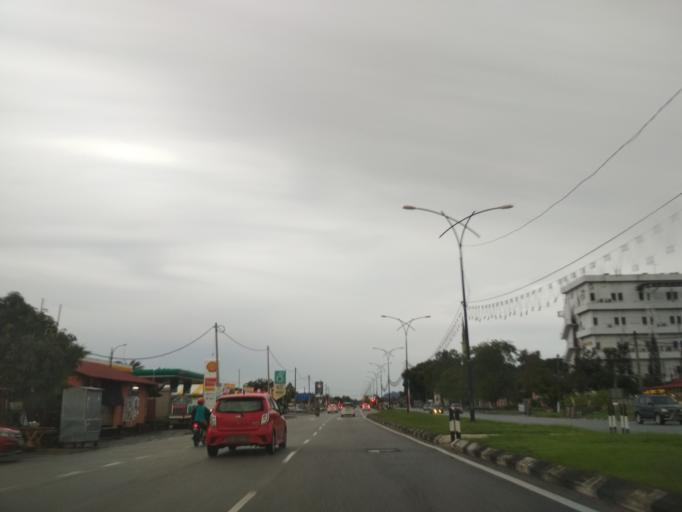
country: MY
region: Perlis
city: Kangar
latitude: 6.4507
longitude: 100.2059
